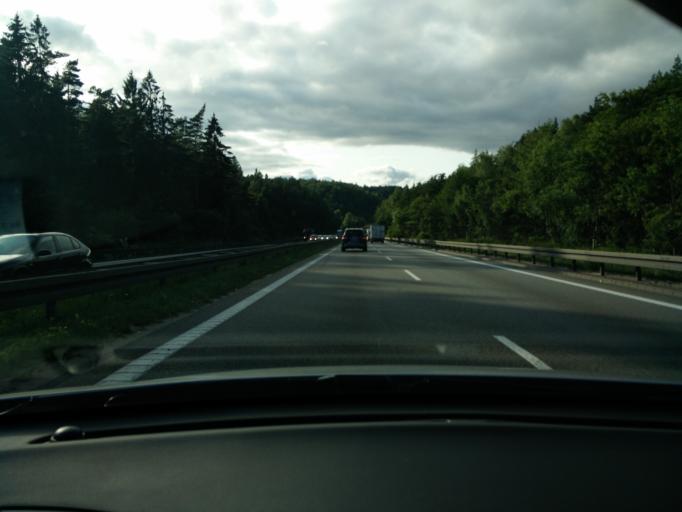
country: PL
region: Pomeranian Voivodeship
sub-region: Gdynia
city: Wielki Kack
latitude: 54.4868
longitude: 18.4682
